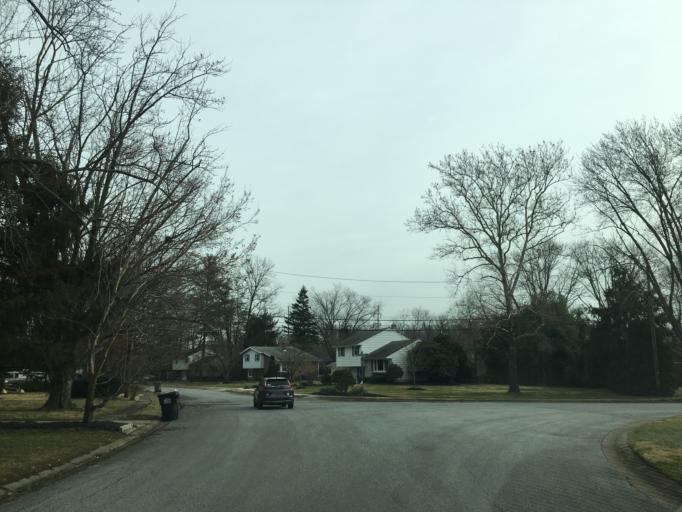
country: US
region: Delaware
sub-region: New Castle County
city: Bellefonte
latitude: 39.7857
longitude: -75.5014
